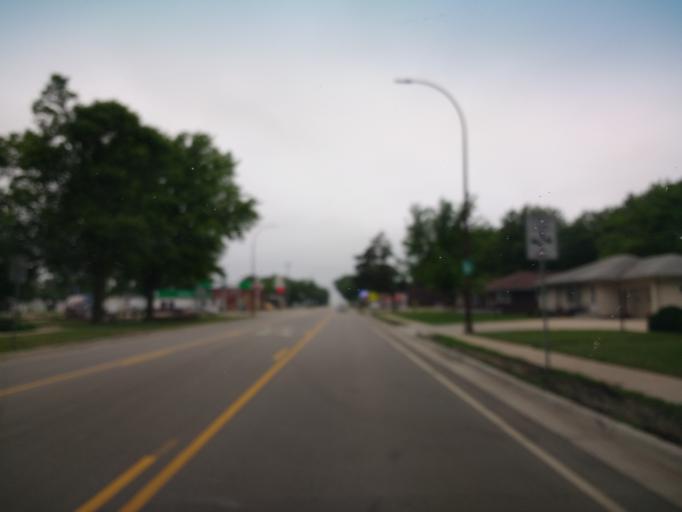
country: US
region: Iowa
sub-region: O'Brien County
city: Sanborn
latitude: 43.1861
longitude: -95.6548
